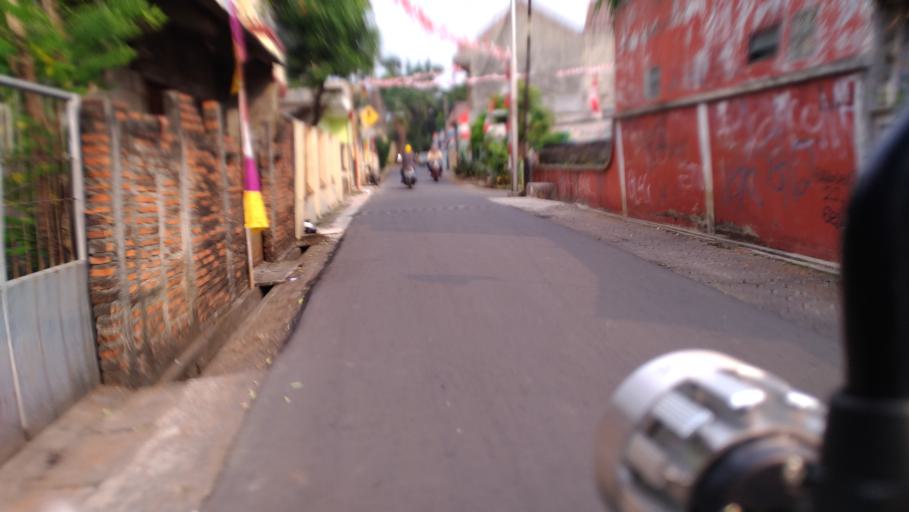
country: ID
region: West Java
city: Depok
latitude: -6.3538
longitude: 106.8829
